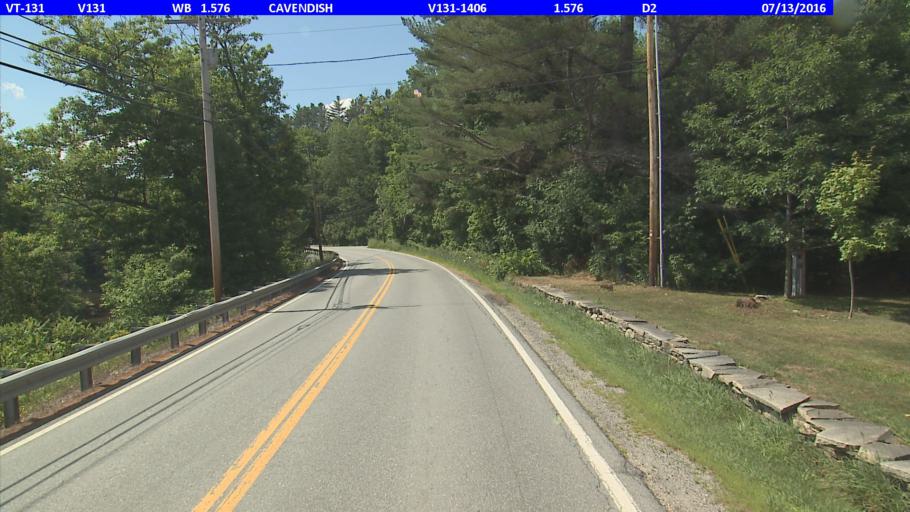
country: US
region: Vermont
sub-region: Windsor County
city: Chester
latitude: 43.3846
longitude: -72.6180
